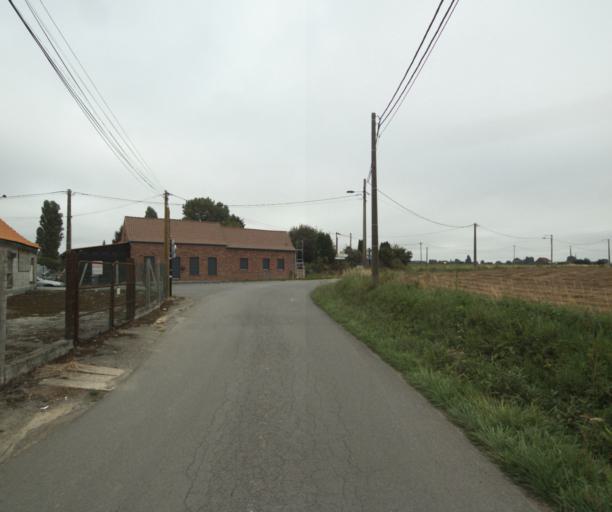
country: FR
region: Nord-Pas-de-Calais
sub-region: Departement du Nord
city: Willems
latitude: 50.6355
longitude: 3.2233
